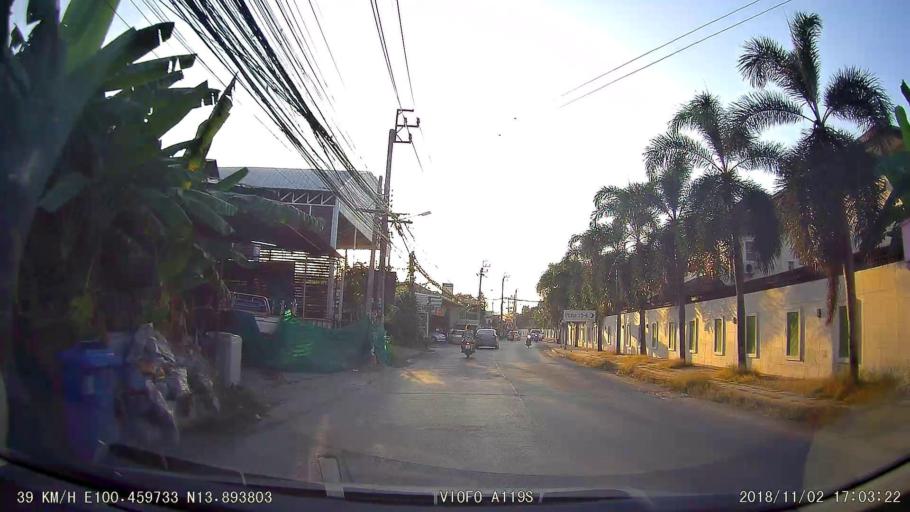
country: TH
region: Nonthaburi
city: Bang Bua Thong
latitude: 13.8938
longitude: 100.4596
